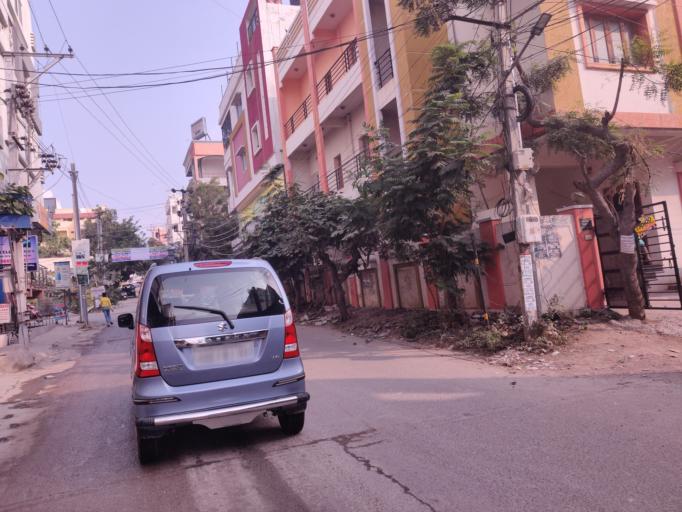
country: IN
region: Telangana
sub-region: Hyderabad
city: Hyderabad
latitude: 17.4037
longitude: 78.3914
